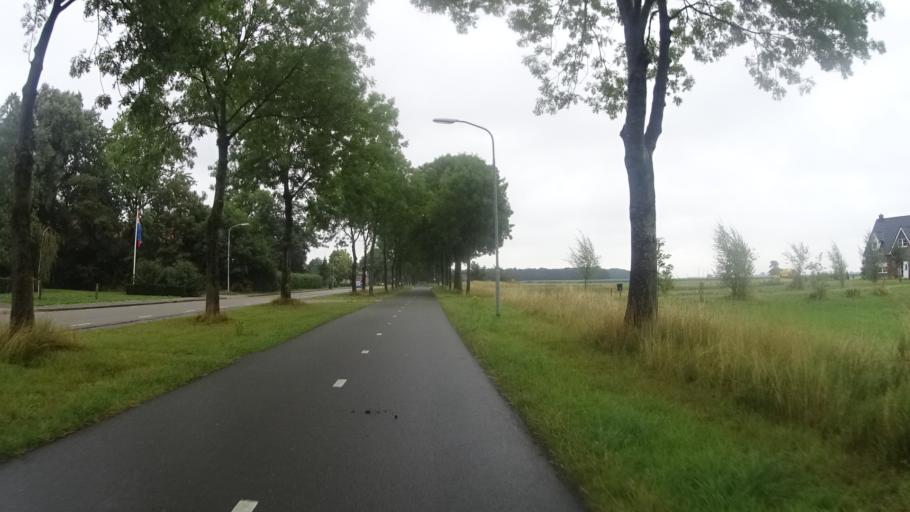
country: NL
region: Groningen
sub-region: Gemeente  Oldambt
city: Winschoten
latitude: 53.1643
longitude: 7.0850
